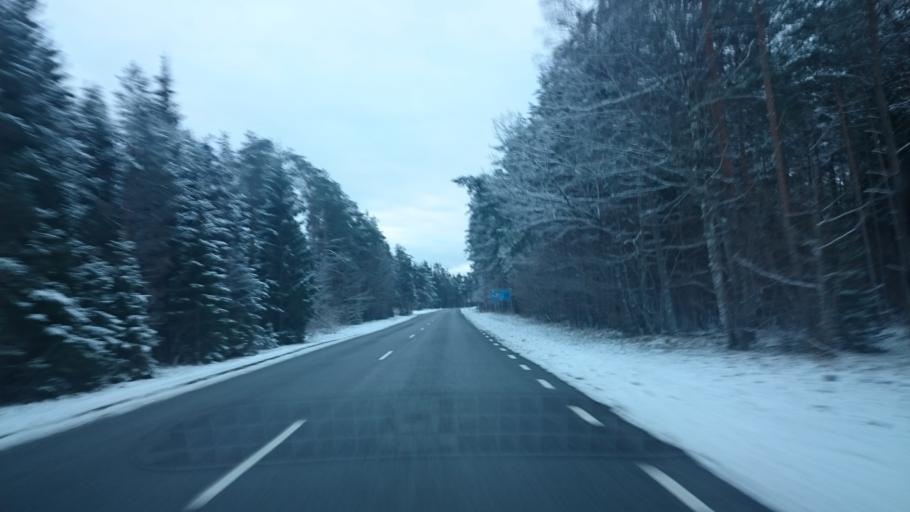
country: EE
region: Saare
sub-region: Kuressaare linn
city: Kuressaare
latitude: 58.3925
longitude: 22.6478
